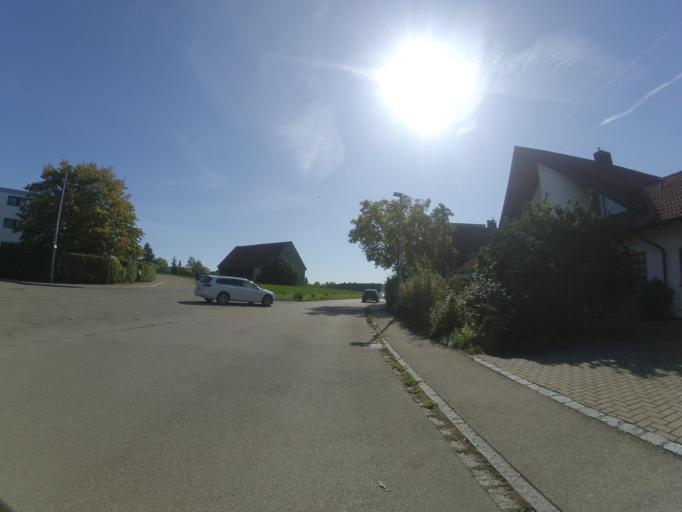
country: DE
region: Baden-Wuerttemberg
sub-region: Tuebingen Region
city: Langenau
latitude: 48.4990
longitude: 10.1107
